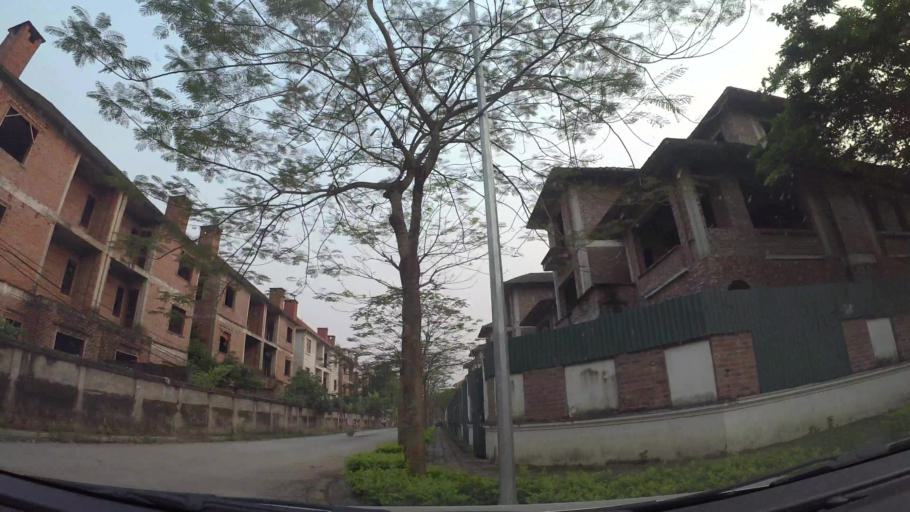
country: VN
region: Ha Noi
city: Cau Dien
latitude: 21.0021
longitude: 105.7294
